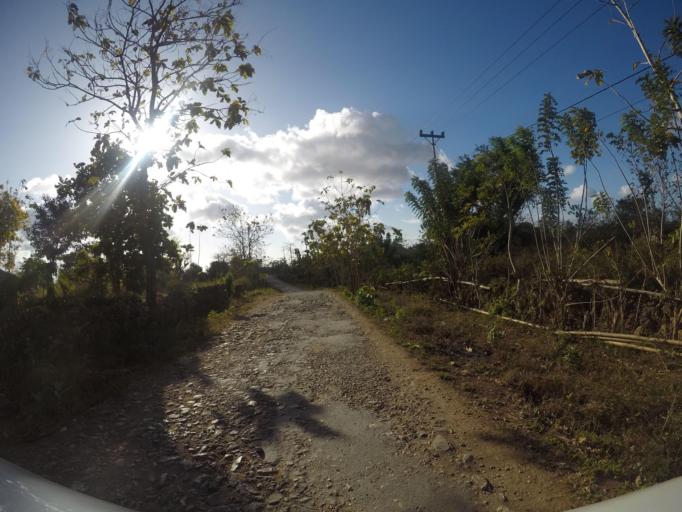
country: TL
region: Lautem
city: Lospalos
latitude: -8.4400
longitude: 126.8609
